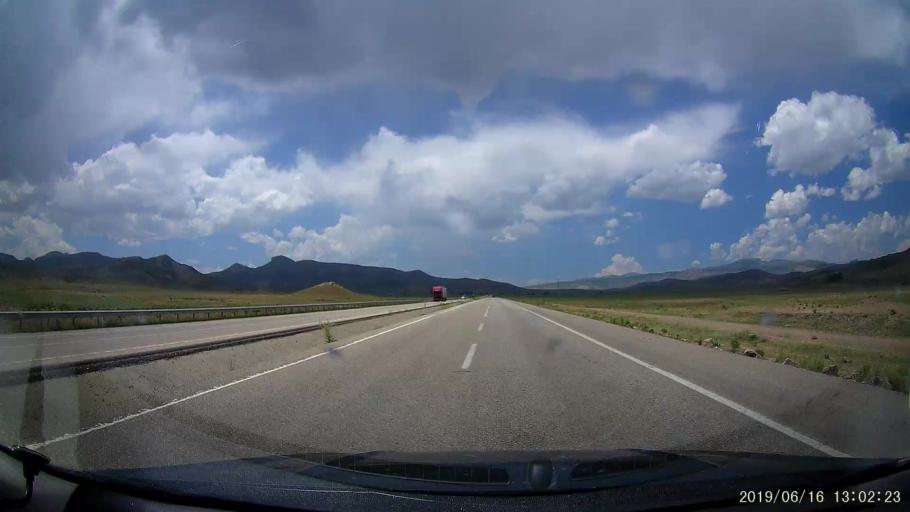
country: TR
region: Agri
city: Sulucem
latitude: 39.5744
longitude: 43.8177
